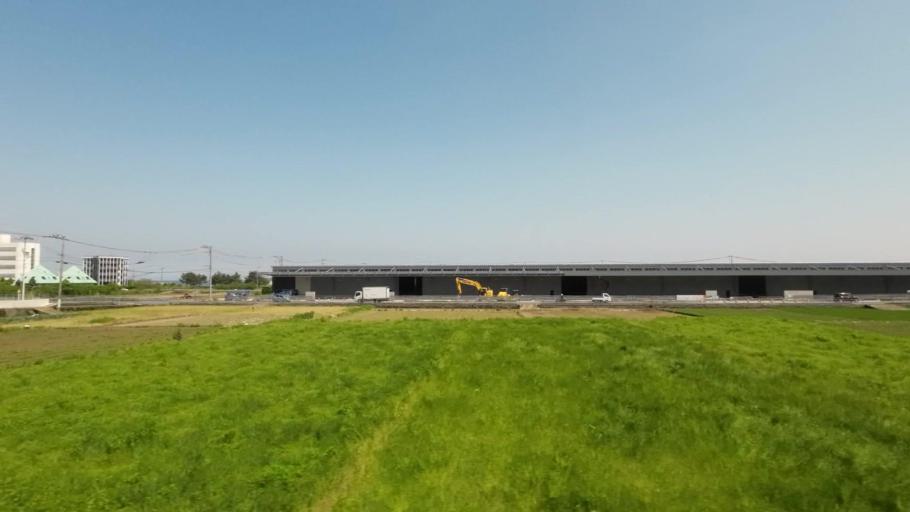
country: JP
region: Ehime
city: Kawanoecho
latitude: 33.9702
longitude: 133.4780
